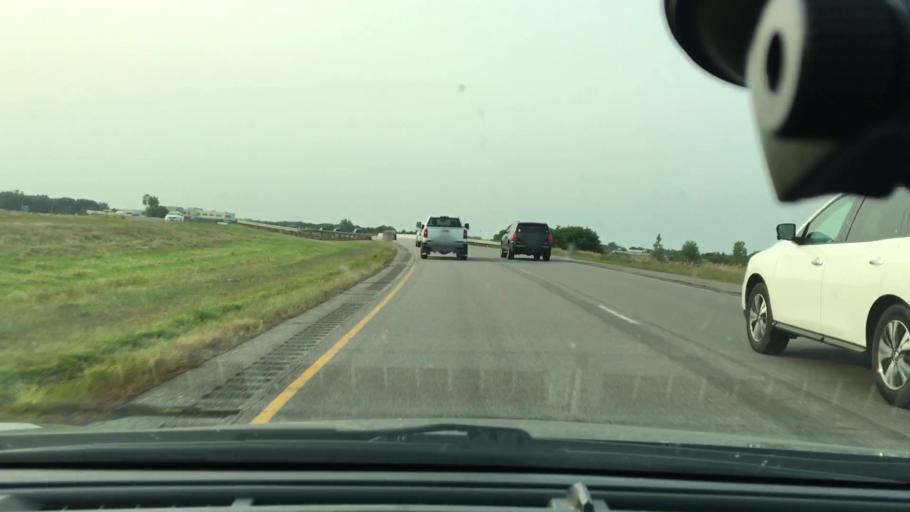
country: US
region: Minnesota
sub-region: Mille Lacs County
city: Princeton
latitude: 45.5525
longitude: -93.5841
